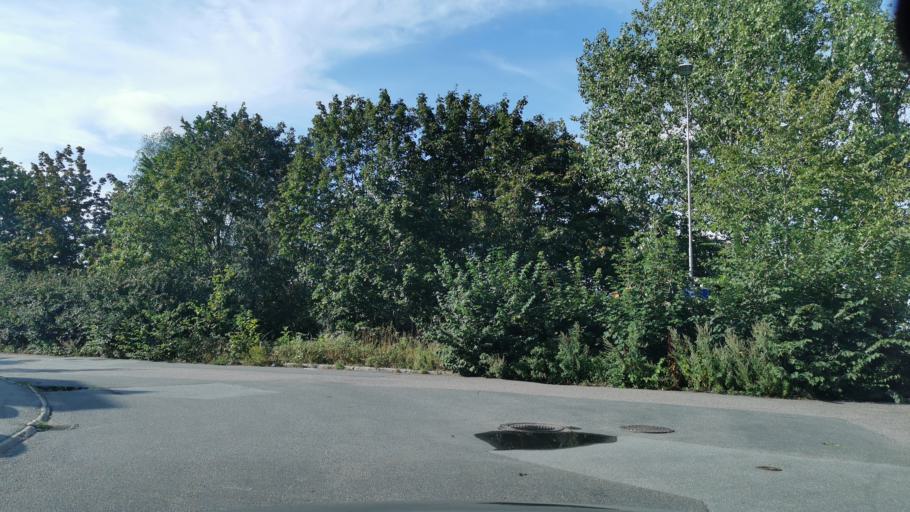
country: SE
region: Vaestra Goetaland
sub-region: Goteborg
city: Majorna
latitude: 57.6593
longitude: 11.9267
